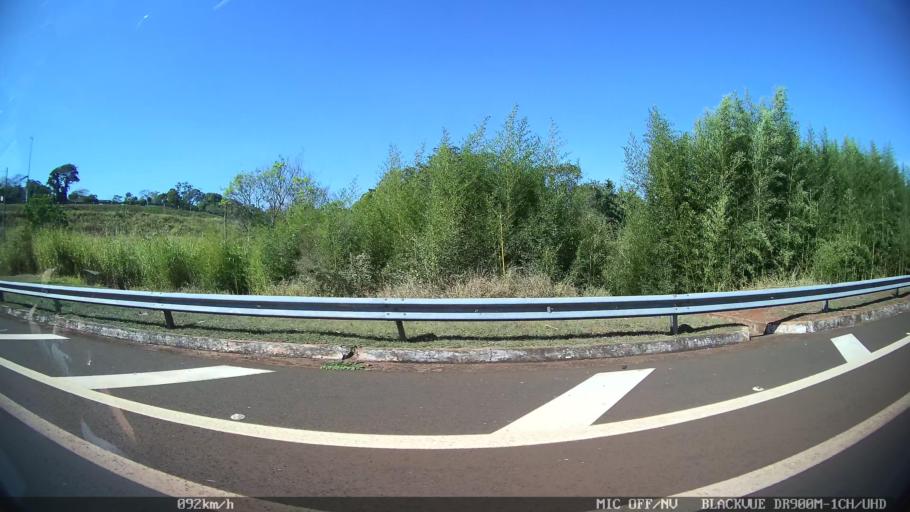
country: BR
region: Sao Paulo
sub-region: Franca
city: Franca
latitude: -20.6351
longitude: -47.4699
